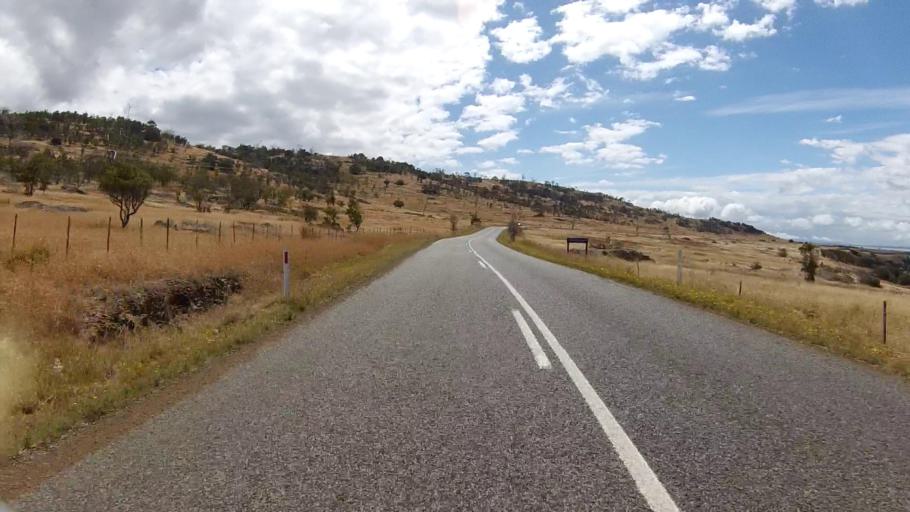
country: AU
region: Tasmania
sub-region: Sorell
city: Sorell
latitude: -42.1830
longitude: 148.0670
